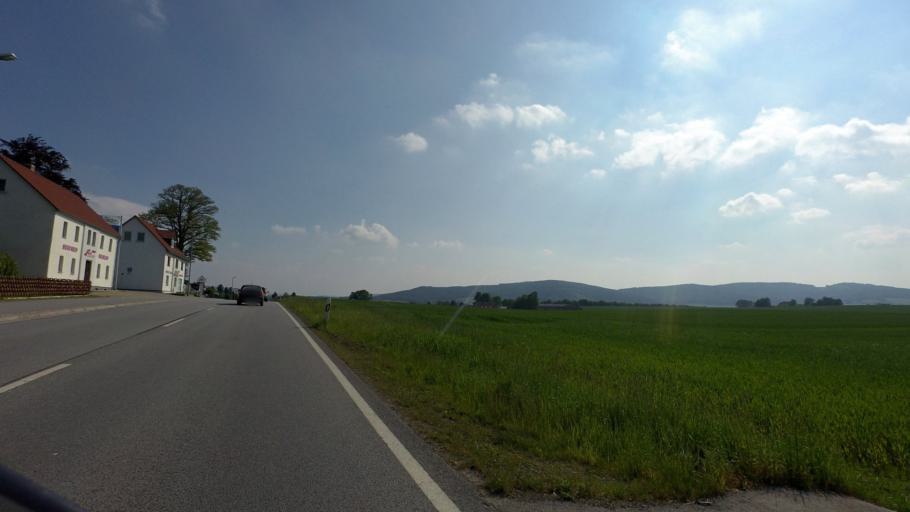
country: DE
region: Saxony
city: Grosspostwitz
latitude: 51.1354
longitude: 14.4415
